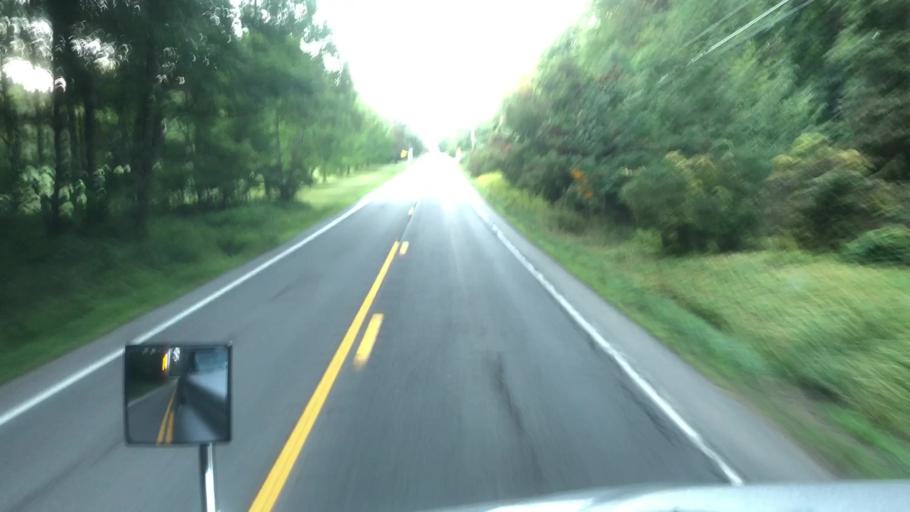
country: US
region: Pennsylvania
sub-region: Crawford County
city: Titusville
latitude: 41.5609
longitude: -79.6111
